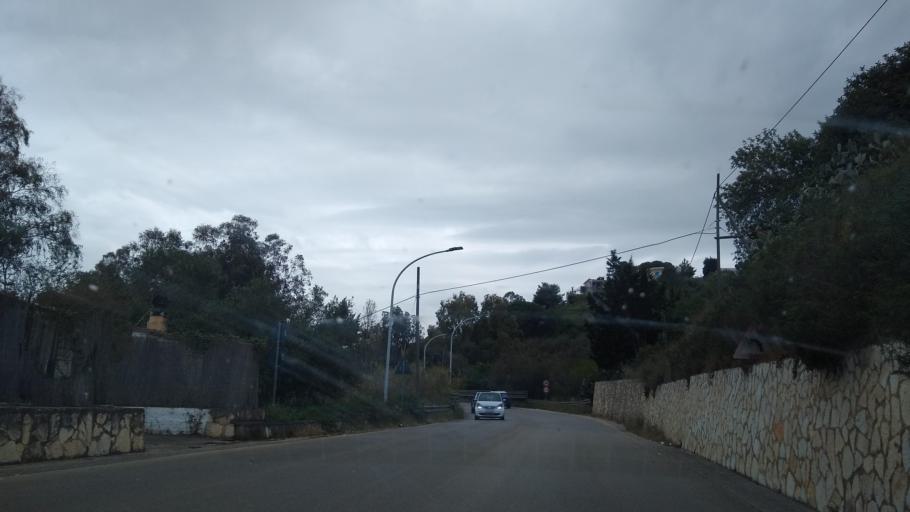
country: IT
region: Sicily
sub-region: Trapani
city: Alcamo
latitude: 38.0253
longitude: 12.9511
